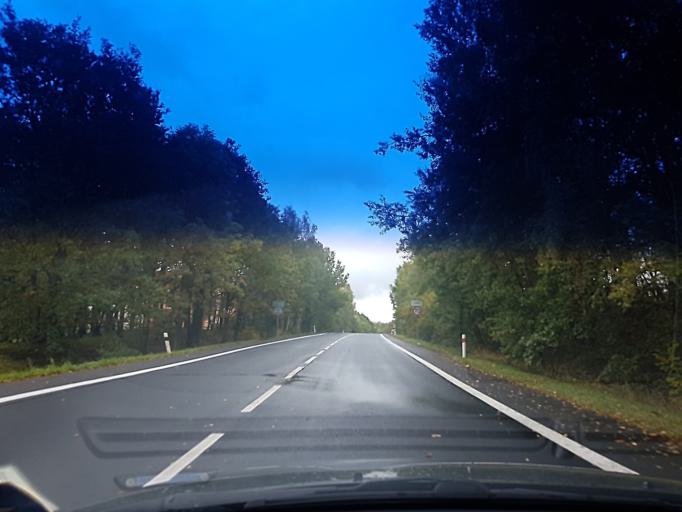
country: CZ
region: Karlovarsky
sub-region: Okres Cheb
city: Cheb
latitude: 50.0759
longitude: 12.3475
